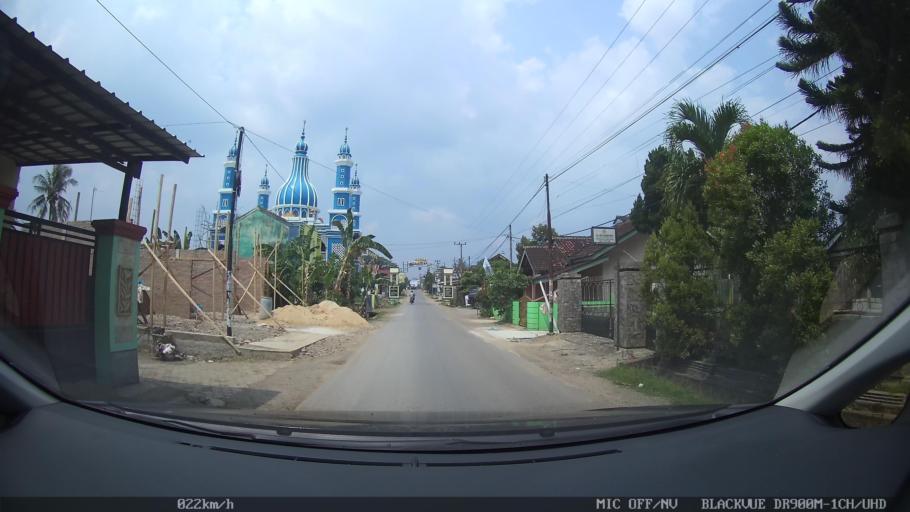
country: ID
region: Lampung
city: Gadingrejo
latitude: -5.3763
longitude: 105.0548
